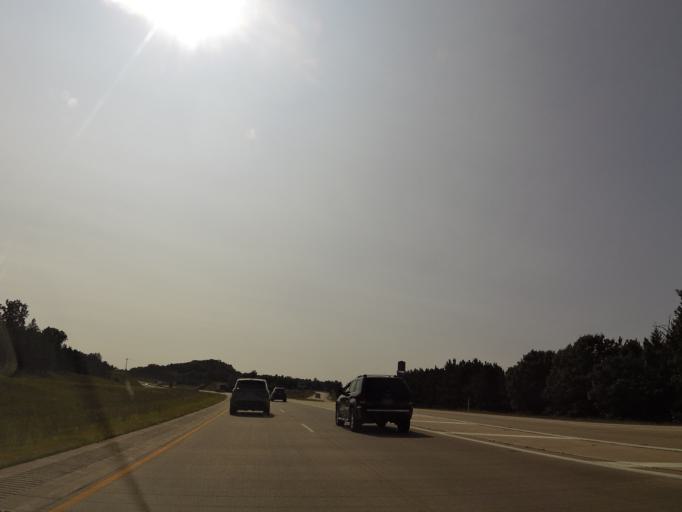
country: US
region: Wisconsin
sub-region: Monroe County
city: Sparta
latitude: 43.9434
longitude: -90.7602
